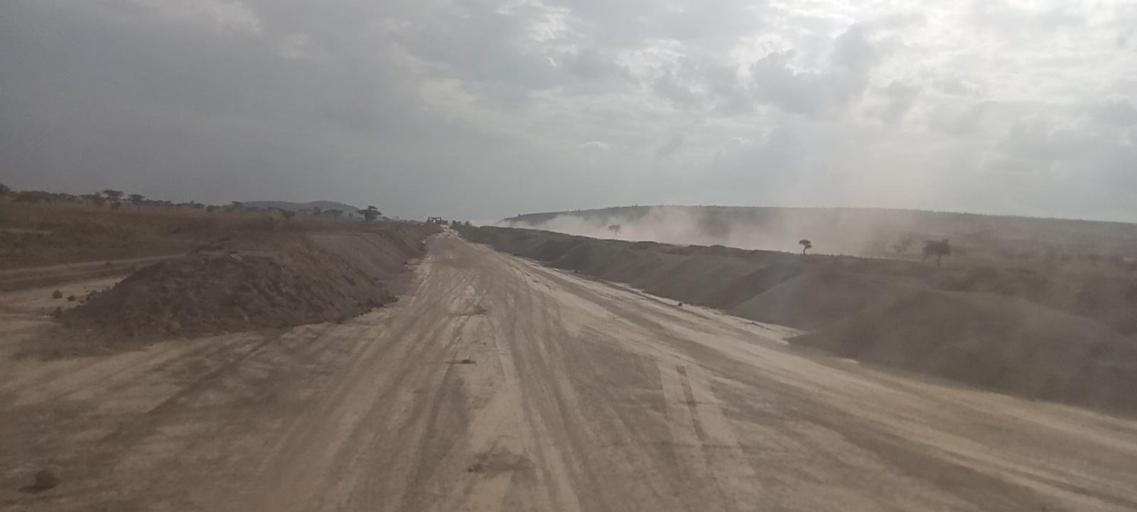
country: ET
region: Oromiya
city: Ziway
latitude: 7.8213
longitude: 38.6472
